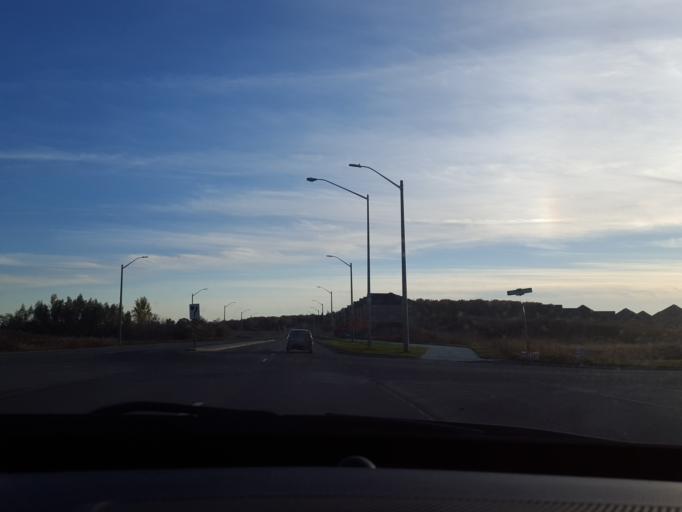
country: CA
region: Ontario
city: Markham
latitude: 43.8888
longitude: -79.2137
